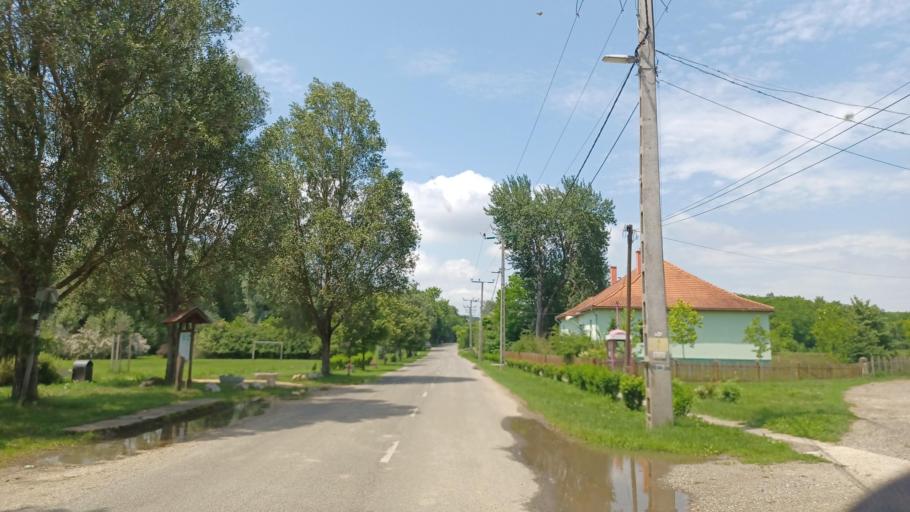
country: HU
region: Tolna
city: Simontornya
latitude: 46.6795
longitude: 18.5349
